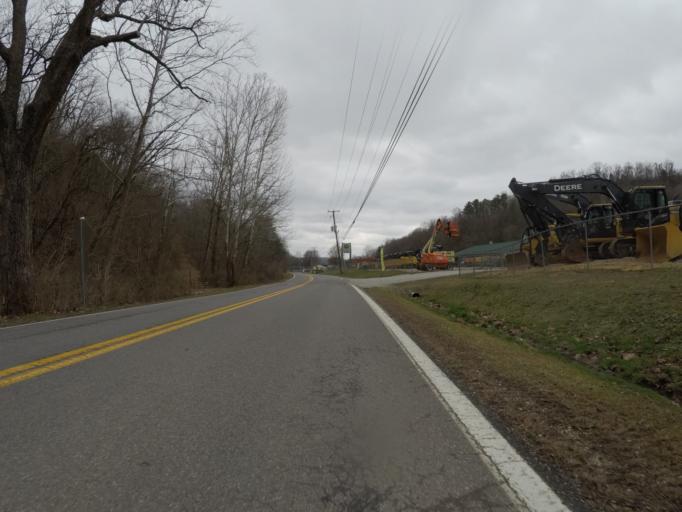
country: US
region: West Virginia
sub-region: Cabell County
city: Barboursville
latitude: 38.4328
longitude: -82.2942
